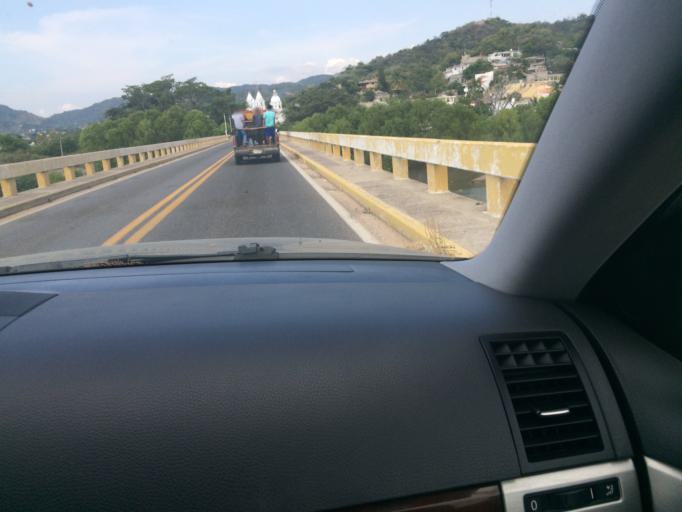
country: MX
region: Jalisco
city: Cihuatlan
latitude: 19.2365
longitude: -104.5538
